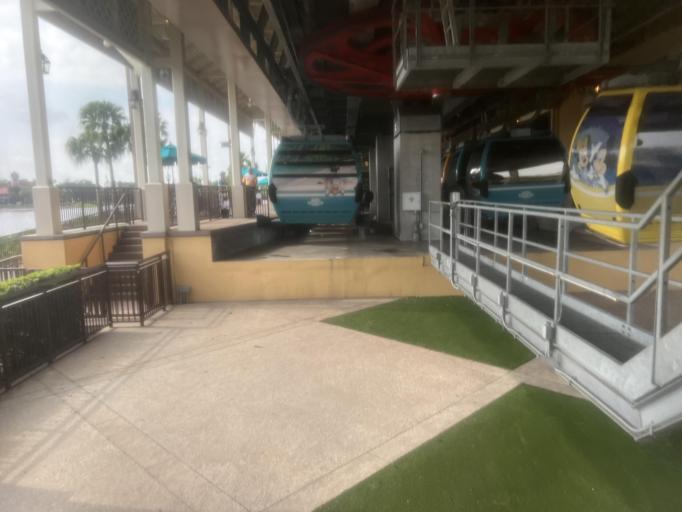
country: US
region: Florida
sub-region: Osceola County
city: Celebration
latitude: 28.3617
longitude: -81.5444
